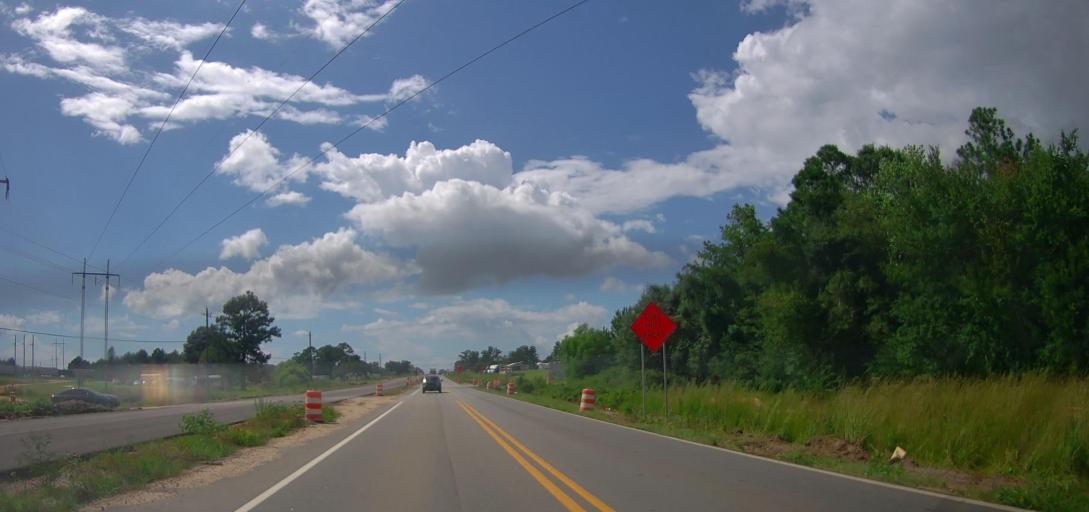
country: US
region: Georgia
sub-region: Coffee County
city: Douglas
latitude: 31.5341
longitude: -82.9164
